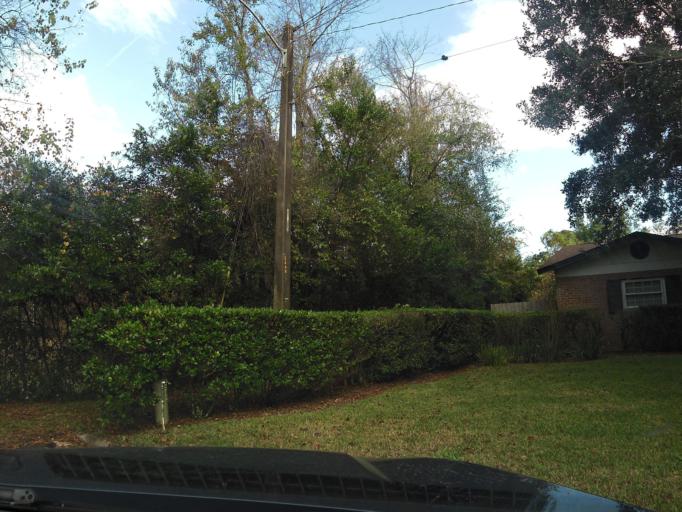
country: US
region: Florida
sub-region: Duval County
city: Jacksonville
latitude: 30.3468
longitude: -81.5616
